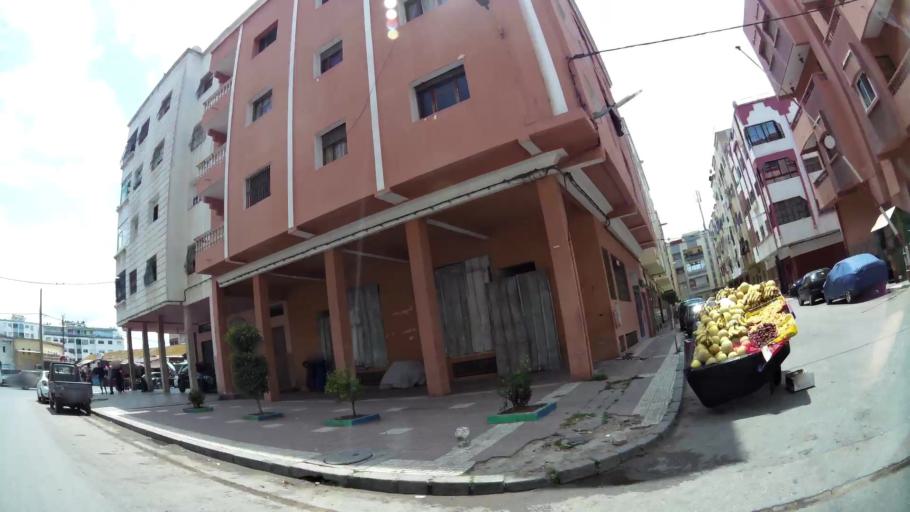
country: MA
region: Rabat-Sale-Zemmour-Zaer
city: Sale
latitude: 34.0439
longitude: -6.8199
